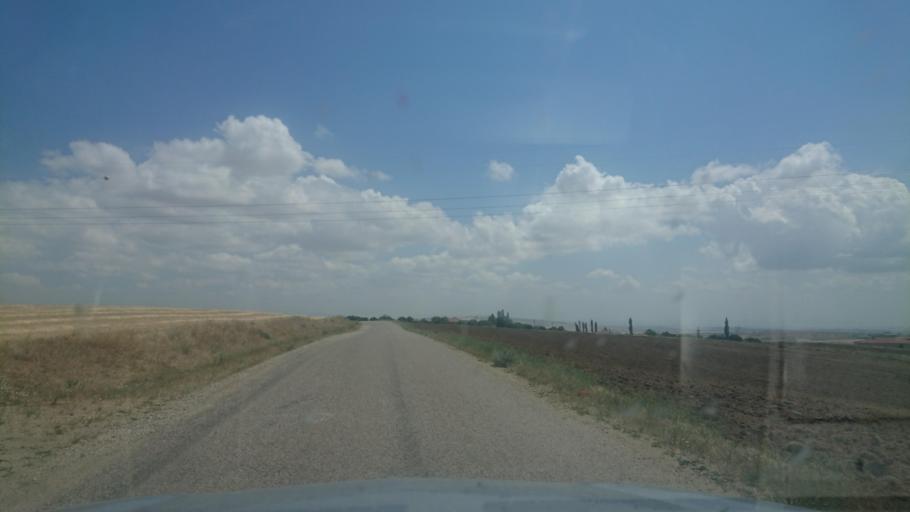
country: TR
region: Aksaray
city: Agacoren
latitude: 38.8693
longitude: 33.9377
